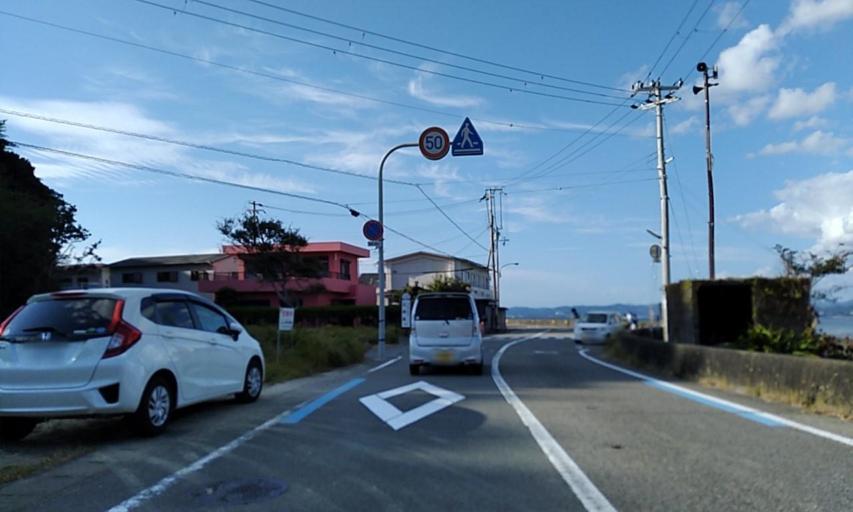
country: JP
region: Wakayama
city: Tanabe
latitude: 33.6934
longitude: 135.3497
